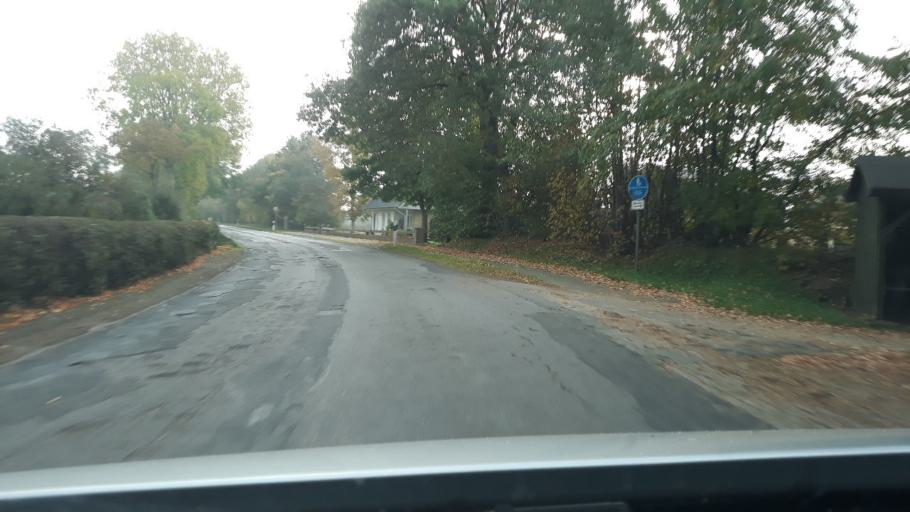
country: DE
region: Schleswig-Holstein
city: Borm
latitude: 54.3990
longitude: 9.3808
